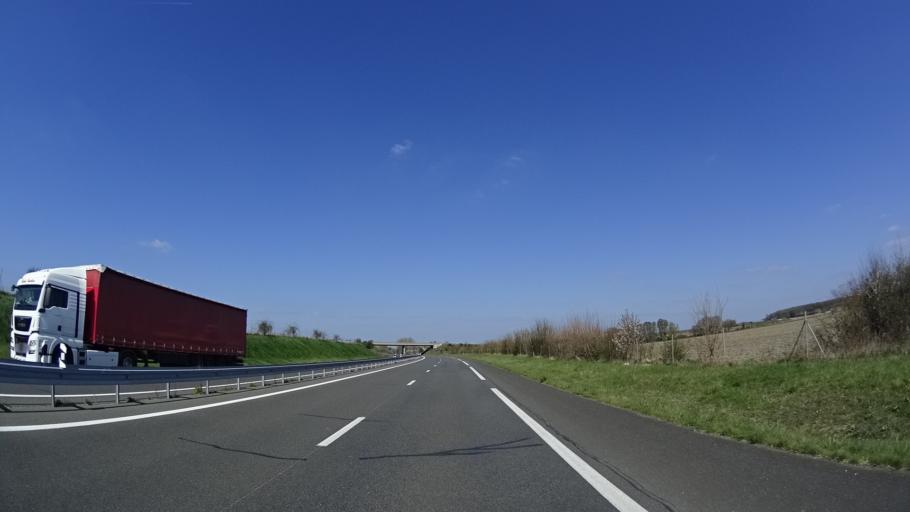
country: FR
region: Pays de la Loire
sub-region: Departement de Maine-et-Loire
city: Saint-Jean
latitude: 47.2701
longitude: -0.3362
